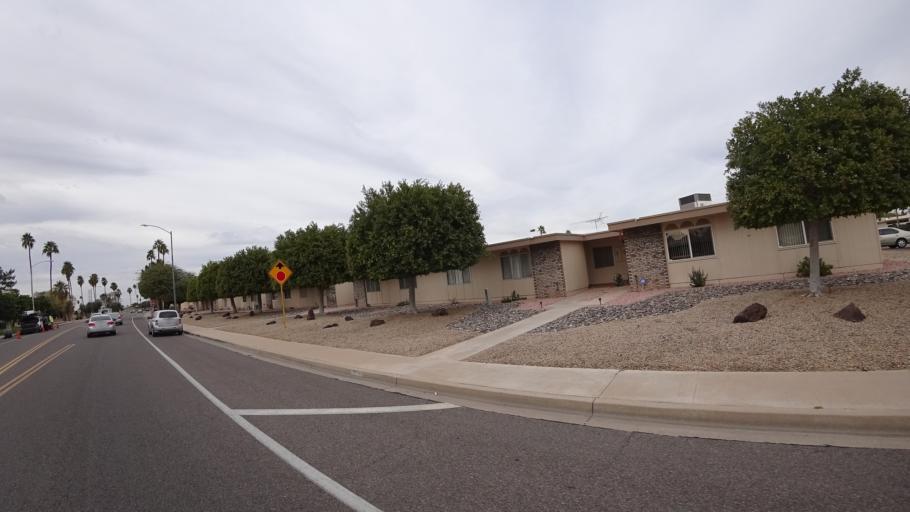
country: US
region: Arizona
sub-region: Maricopa County
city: Youngtown
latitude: 33.6083
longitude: -112.2965
